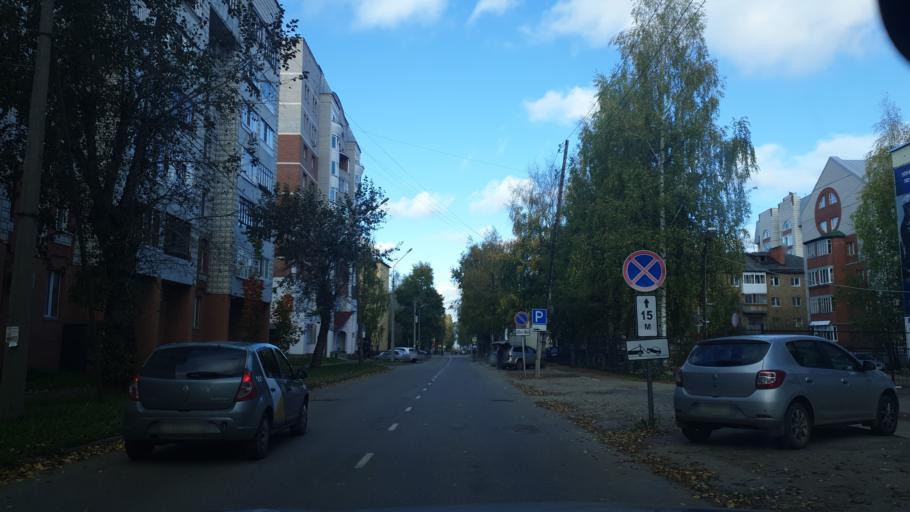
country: RU
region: Komi Republic
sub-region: Syktyvdinskiy Rayon
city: Syktyvkar
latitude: 61.6643
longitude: 50.8452
